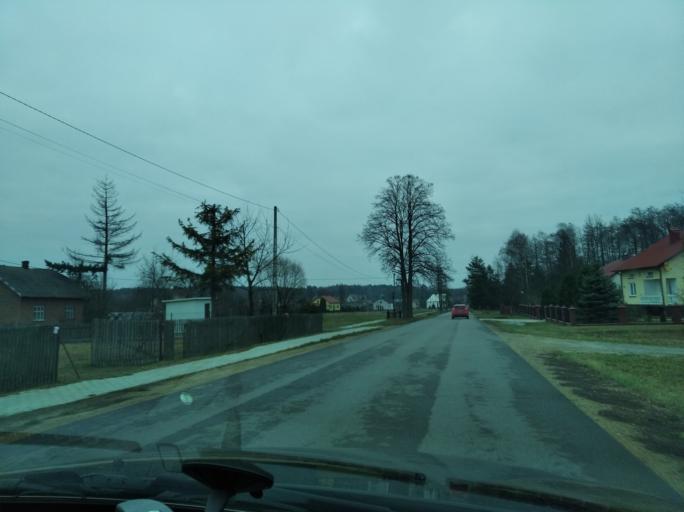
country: PL
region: Subcarpathian Voivodeship
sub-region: Powiat lancucki
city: Rakszawa
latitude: 50.1624
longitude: 22.1915
